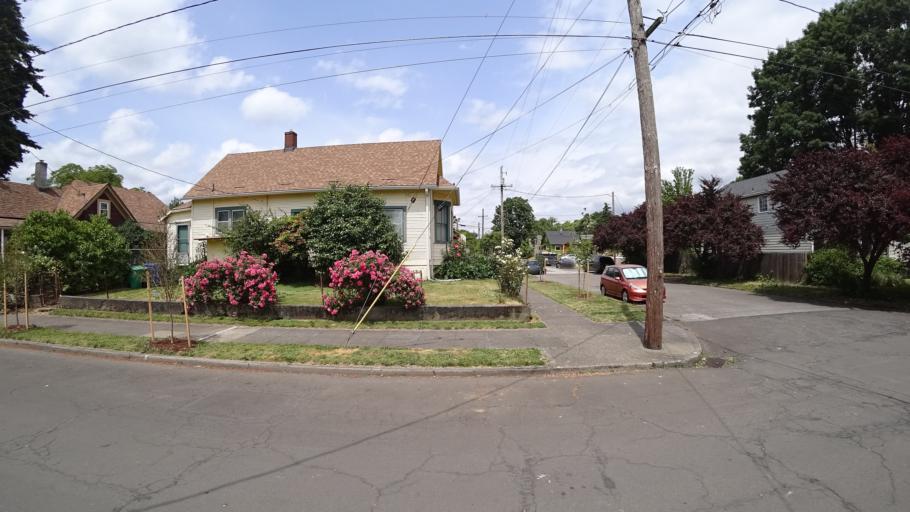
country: US
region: Oregon
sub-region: Multnomah County
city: Portland
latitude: 45.4961
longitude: -122.6505
